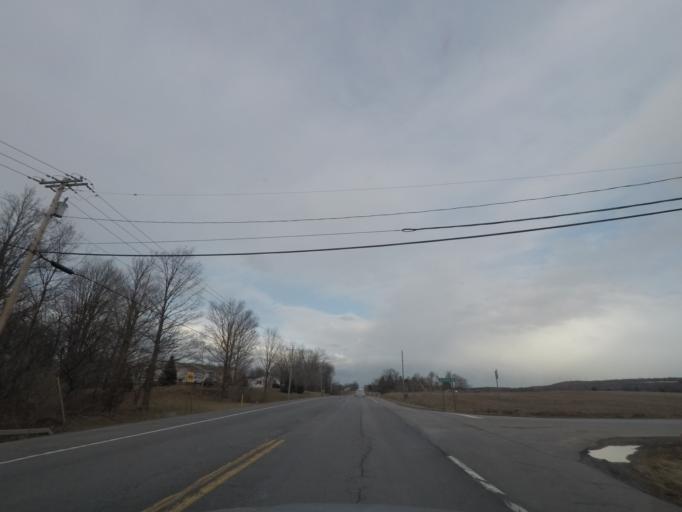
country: US
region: New York
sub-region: Oneida County
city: Vernon
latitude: 43.0730
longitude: -75.4787
